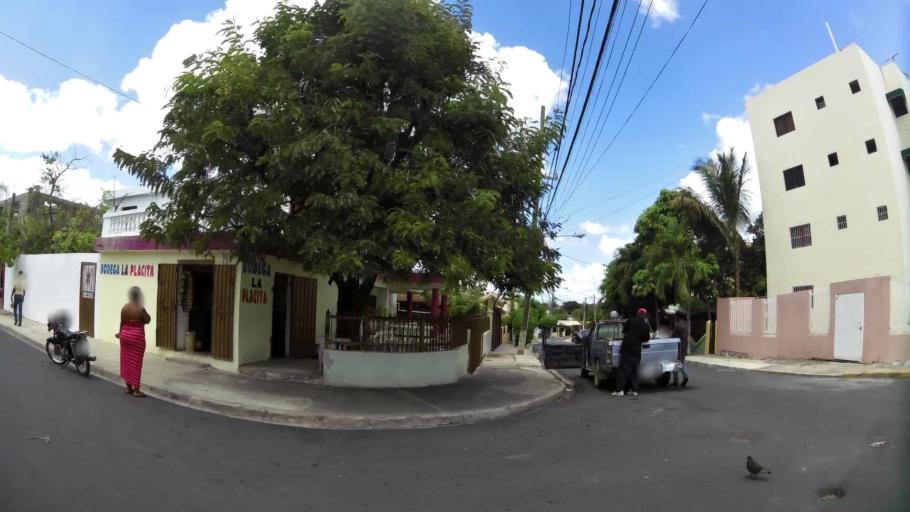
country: DO
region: Nacional
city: Ensanche Luperon
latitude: 18.5176
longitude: -69.9082
